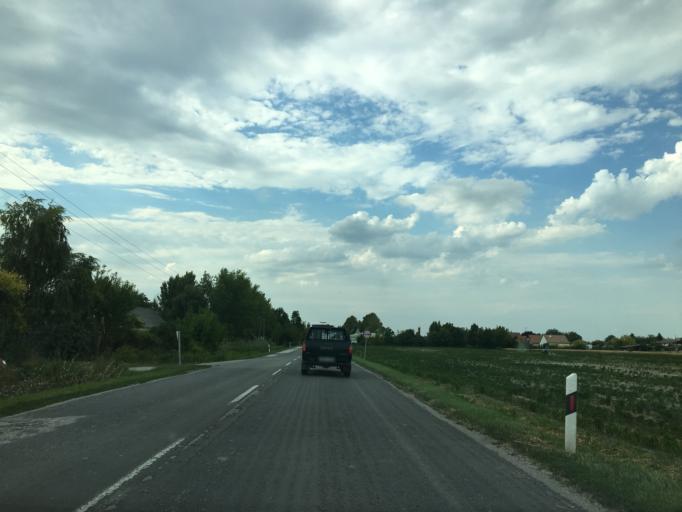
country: HU
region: Bacs-Kiskun
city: Dusnok
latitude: 46.3758
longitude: 18.9614
